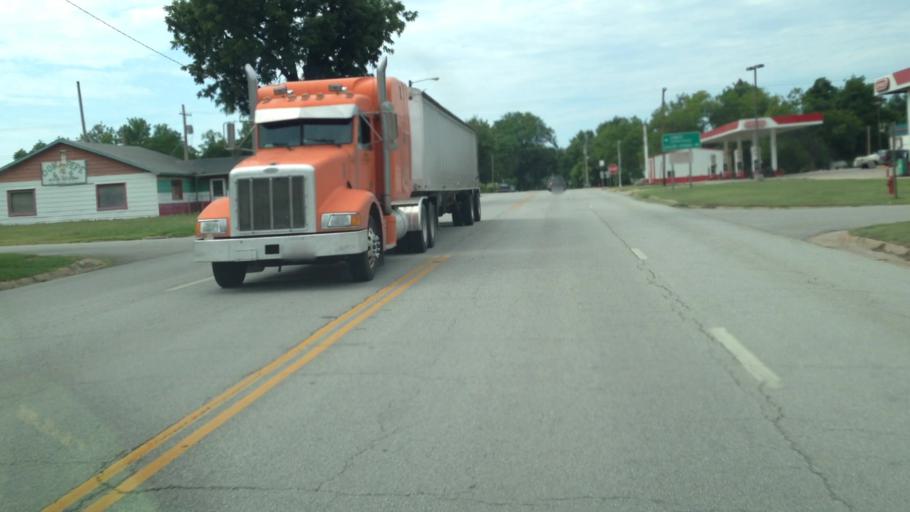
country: US
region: Kansas
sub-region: Labette County
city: Chetopa
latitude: 37.0356
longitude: -95.0861
